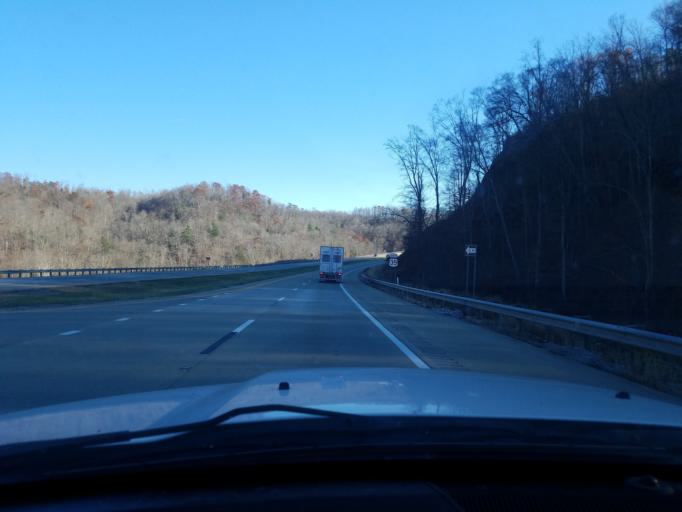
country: US
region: West Virginia
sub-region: Putnam County
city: Eleanor
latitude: 38.5259
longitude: -81.9387
